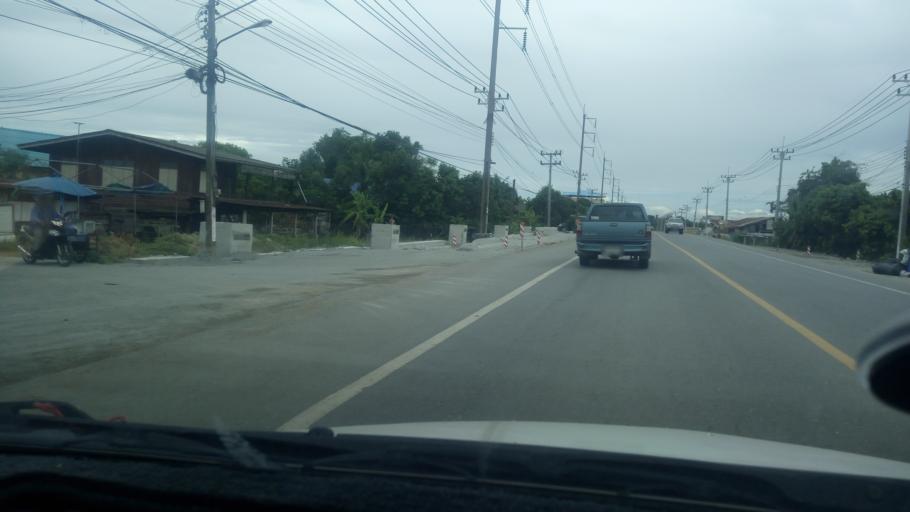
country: TH
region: Chon Buri
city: Phanat Nikhom
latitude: 13.5125
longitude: 101.1563
